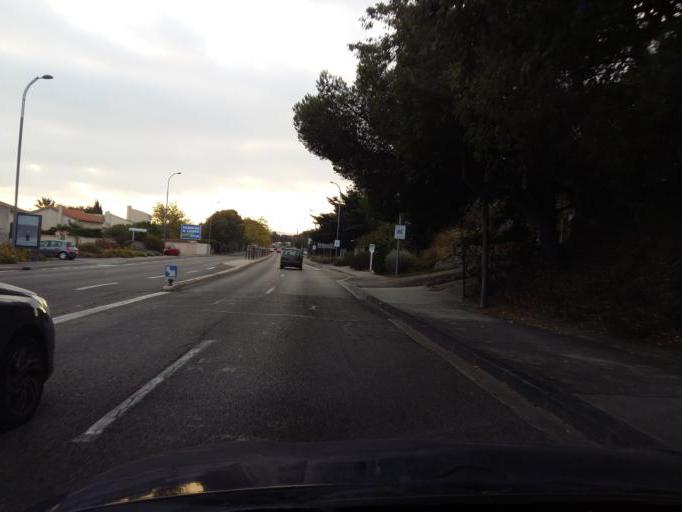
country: FR
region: Provence-Alpes-Cote d'Azur
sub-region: Departement des Bouches-du-Rhone
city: Martigues
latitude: 43.4245
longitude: 5.0539
